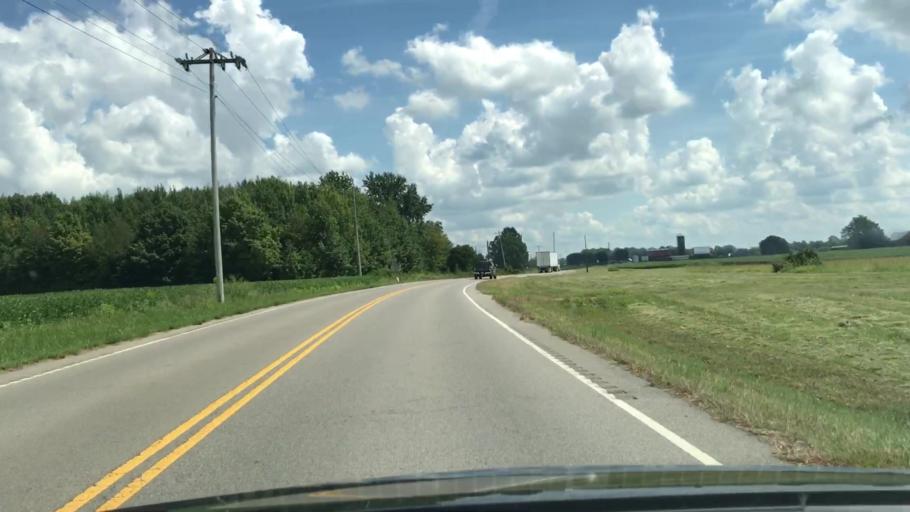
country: US
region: Tennessee
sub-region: Robertson County
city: Springfield
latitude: 36.5556
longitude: -86.7988
